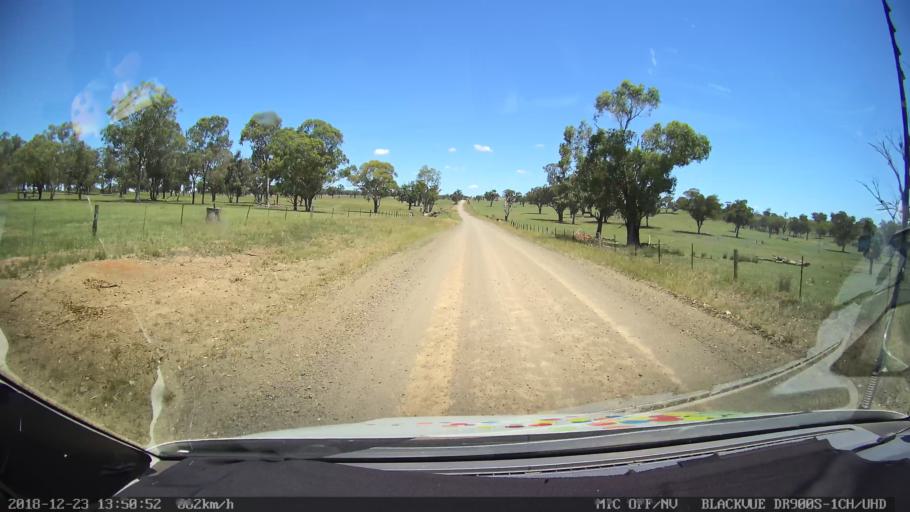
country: AU
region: New South Wales
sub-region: Tamworth Municipality
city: Manilla
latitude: -30.5343
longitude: 151.1060
